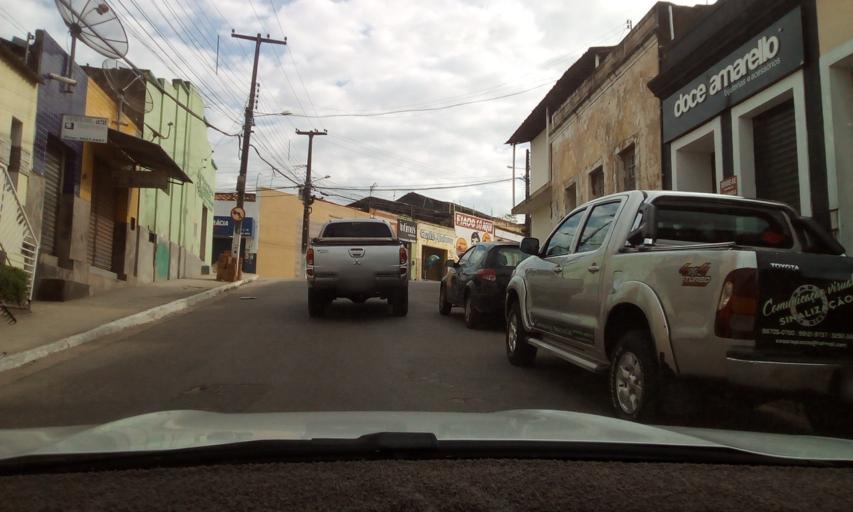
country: BR
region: Paraiba
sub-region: Mamanguape
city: Mamanguape
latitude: -6.8353
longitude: -35.1223
